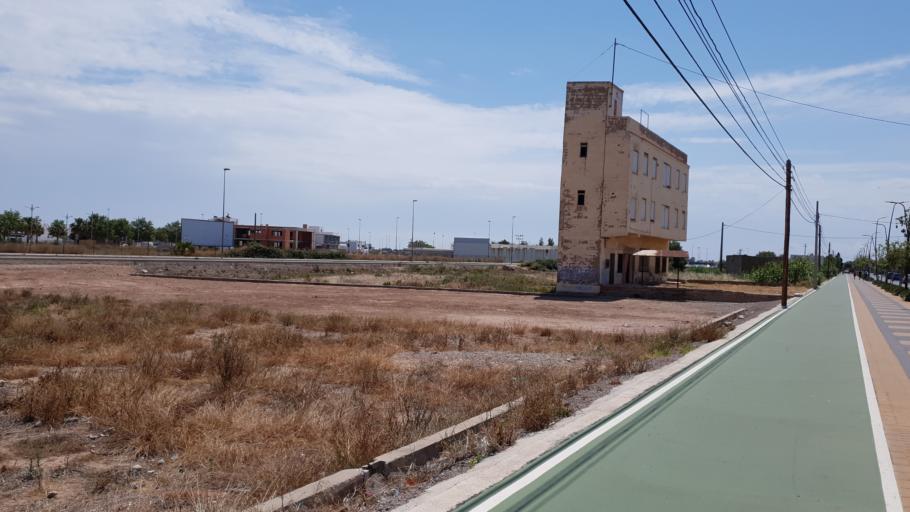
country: ES
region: Valencia
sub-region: Provincia de Castello
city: Burriana
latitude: 39.8818
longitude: -0.0801
